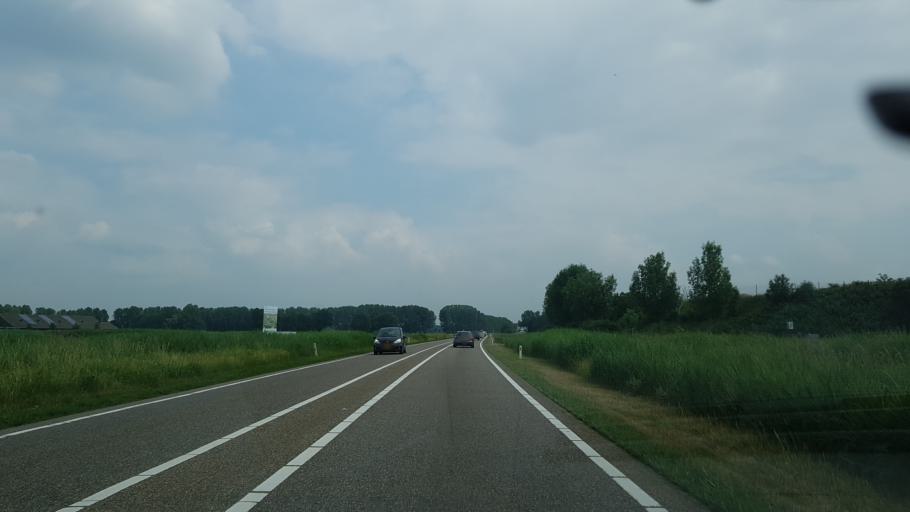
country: NL
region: North Brabant
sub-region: Gemeente Laarbeek
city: Aarle-Rixtel
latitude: 51.5499
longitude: 5.6363
